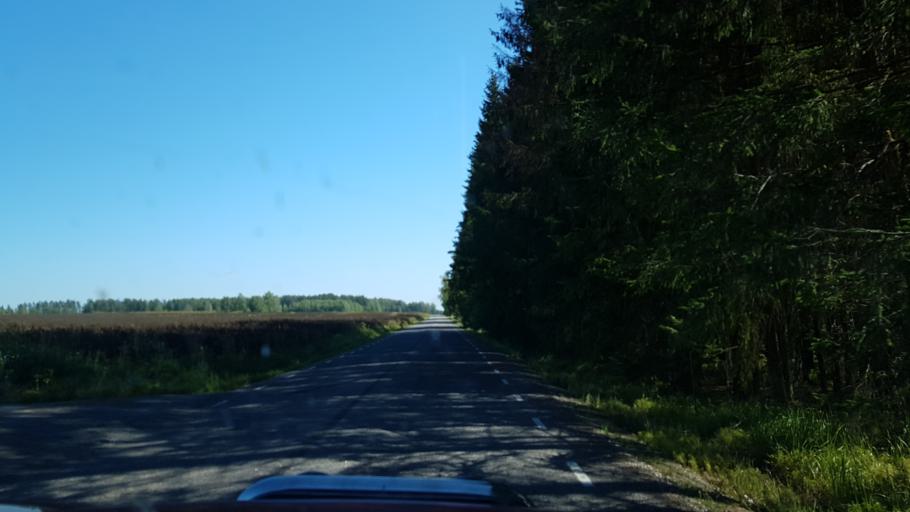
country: EE
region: Polvamaa
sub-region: Polva linn
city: Polva
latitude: 58.2110
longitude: 27.1515
